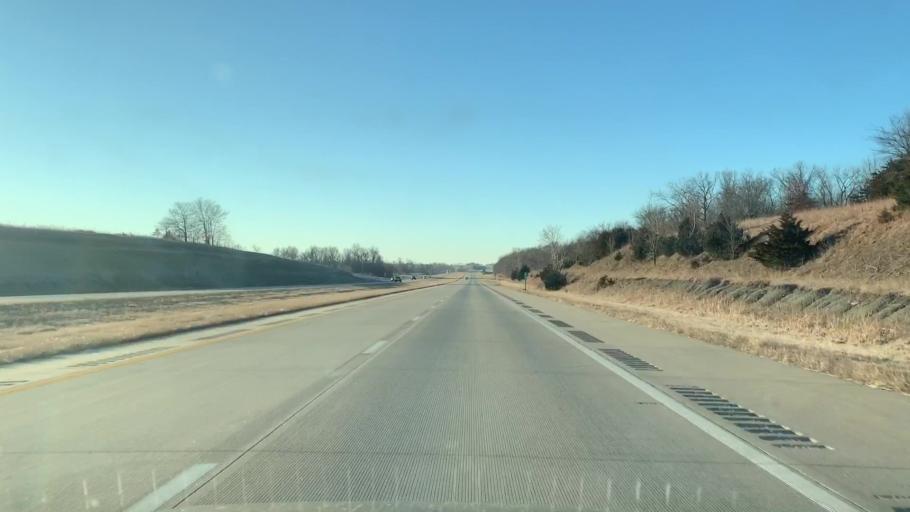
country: US
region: Kansas
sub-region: Linn County
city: Pleasanton
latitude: 38.0222
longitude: -94.7038
